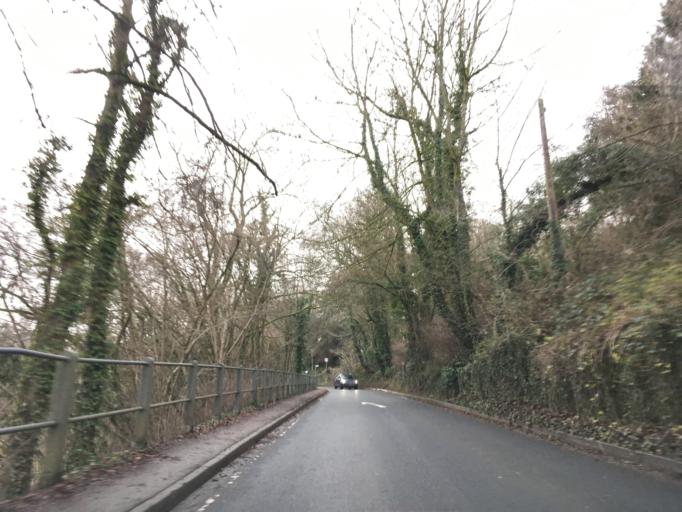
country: GB
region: England
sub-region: Gloucestershire
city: Nailsworth
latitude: 51.6864
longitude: -2.2272
